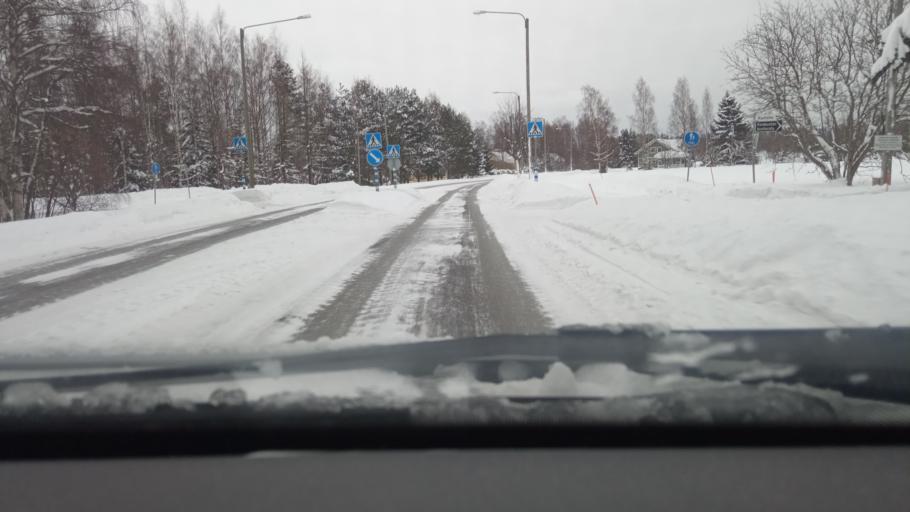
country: FI
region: Southern Ostrobothnia
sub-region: Jaerviseutu
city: Alajaervi
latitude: 62.9932
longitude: 23.8318
